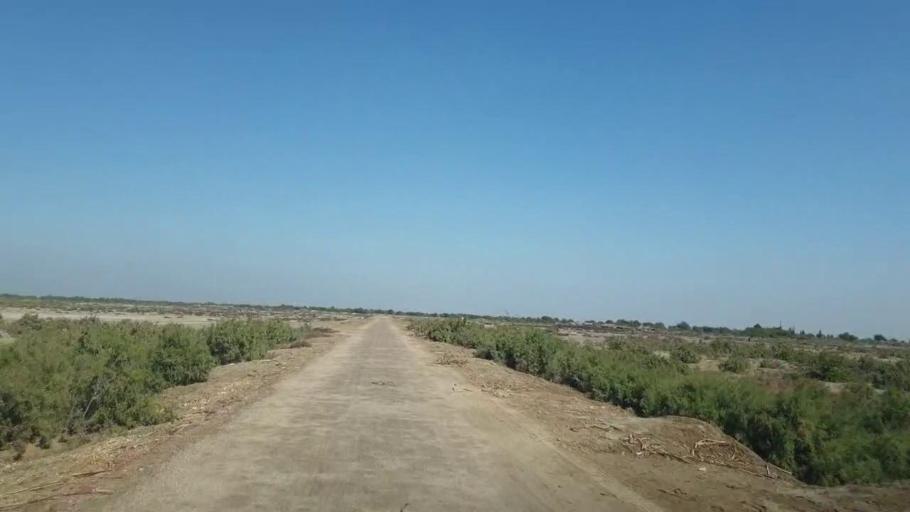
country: PK
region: Sindh
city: Mirpur Khas
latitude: 25.6023
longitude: 69.1281
